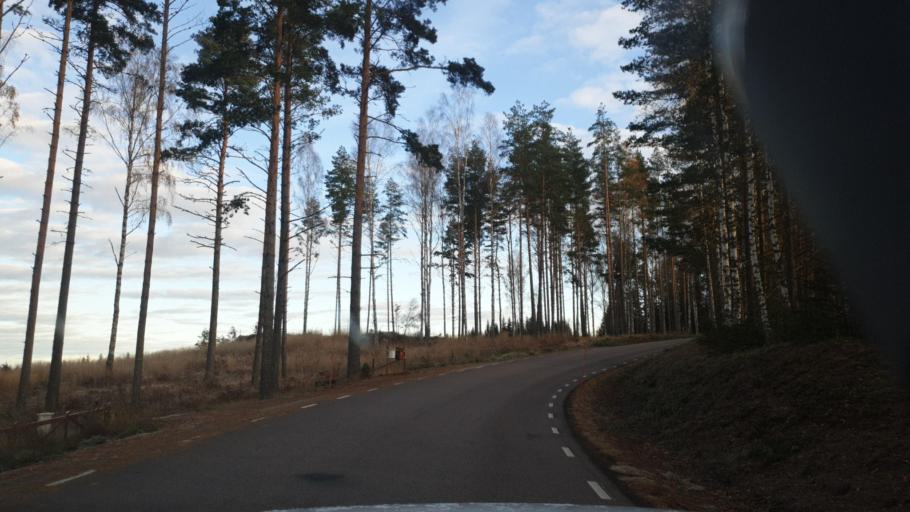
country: SE
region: Vaermland
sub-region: Eda Kommun
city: Charlottenberg
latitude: 59.7905
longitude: 12.2244
